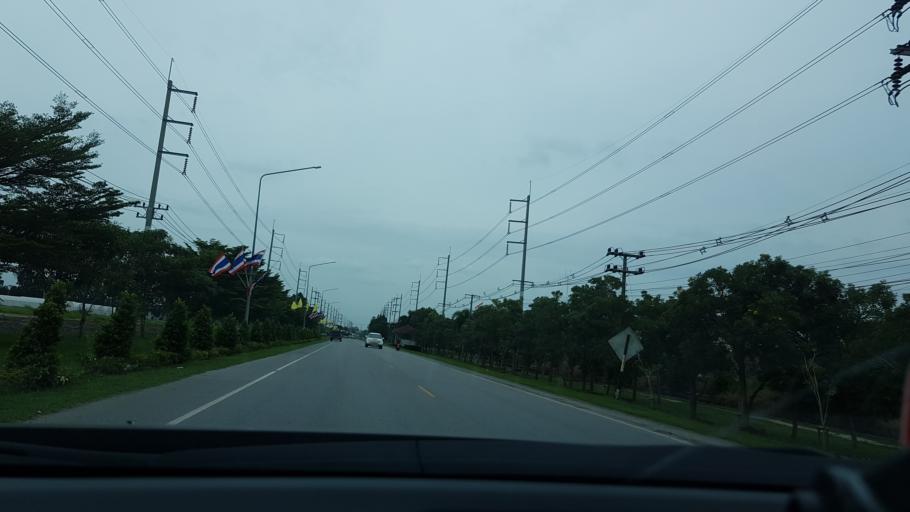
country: TH
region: Phra Nakhon Si Ayutthaya
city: Bang Pa-in
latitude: 14.1686
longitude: 100.5243
